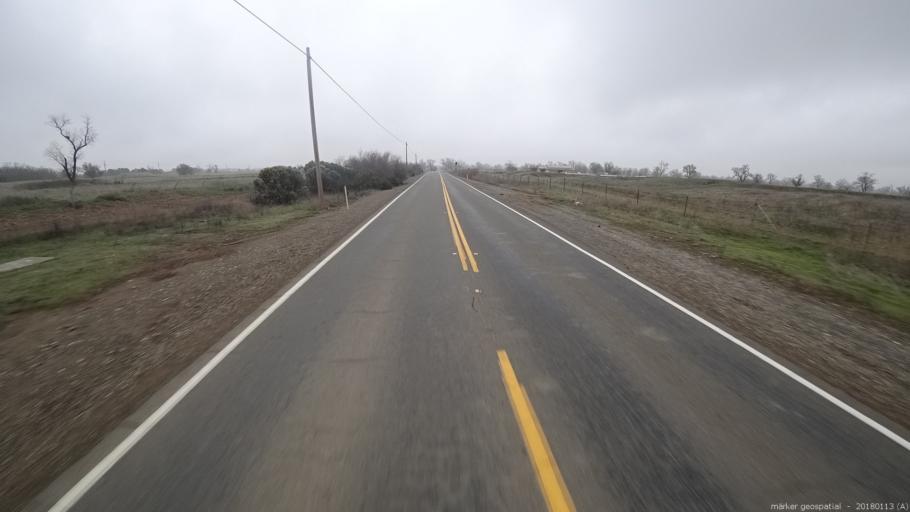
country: US
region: California
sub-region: Sacramento County
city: Gold River
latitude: 38.5924
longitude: -121.2276
